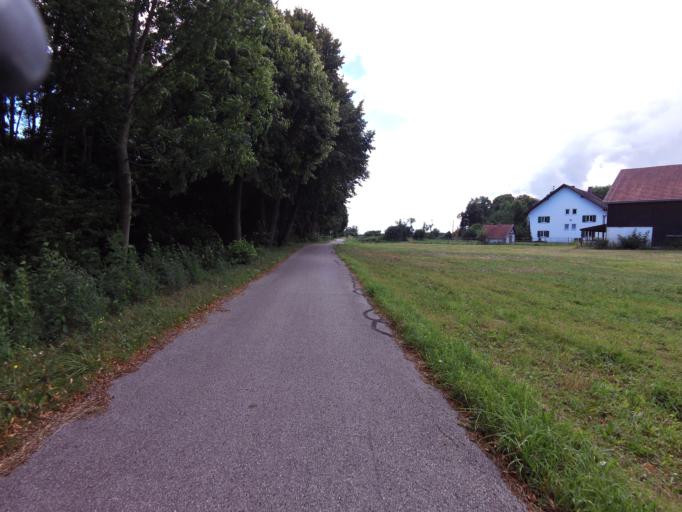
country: DE
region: Bavaria
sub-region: Upper Bavaria
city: Hallbergmoos
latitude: 48.3416
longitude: 11.7334
